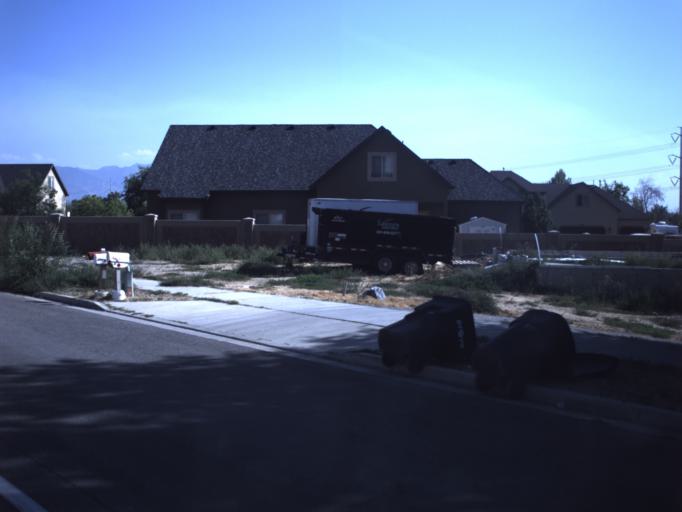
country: US
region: Utah
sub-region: Utah County
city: Orem
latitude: 40.2506
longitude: -111.7040
